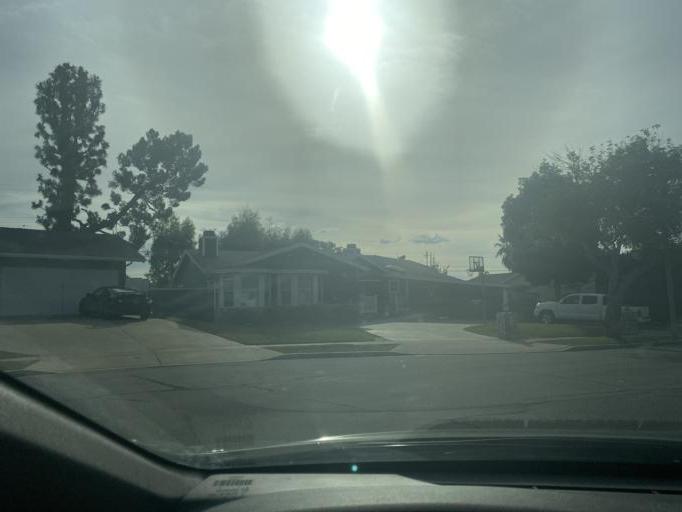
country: US
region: California
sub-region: Orange County
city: Brea
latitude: 33.9074
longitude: -117.8929
